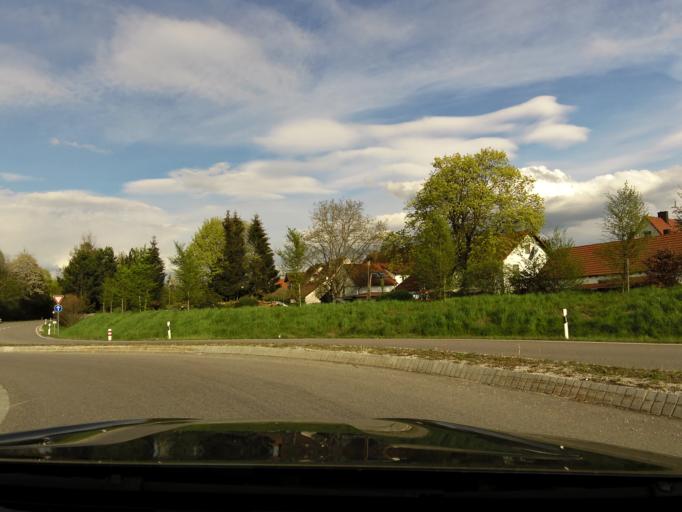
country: DE
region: Bavaria
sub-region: Upper Bavaria
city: Moosburg
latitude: 48.4595
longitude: 11.9227
